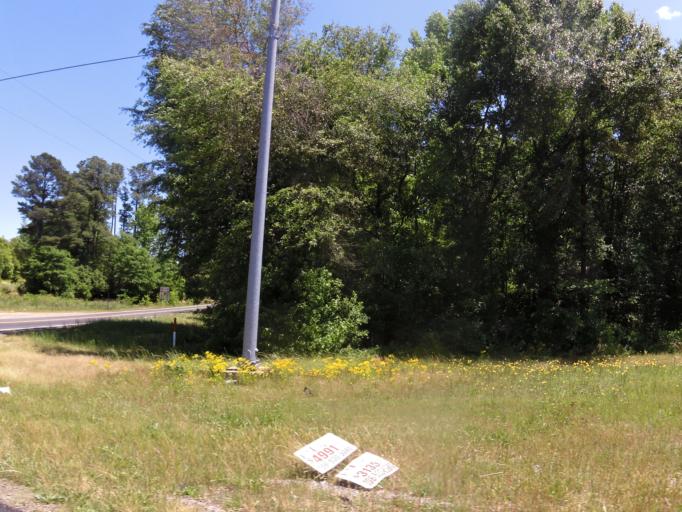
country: US
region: South Carolina
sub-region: Aiken County
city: Clearwater
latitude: 33.4929
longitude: -81.9169
